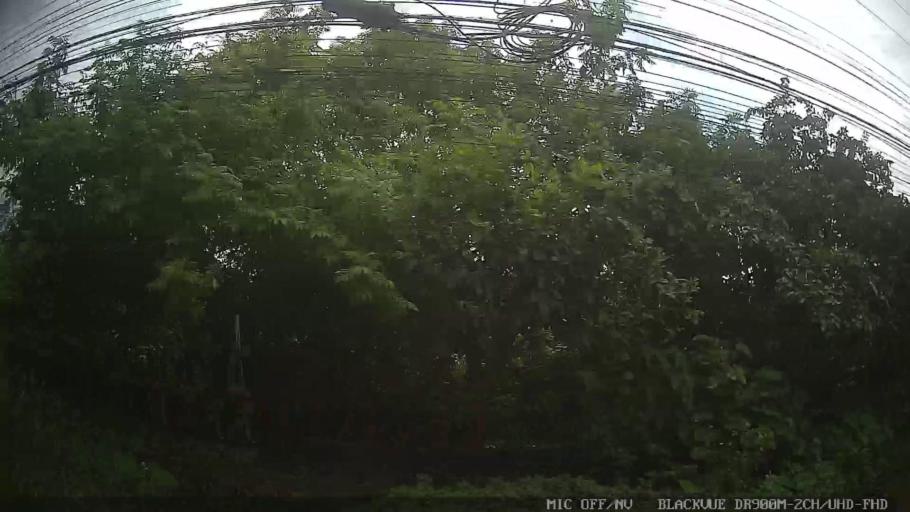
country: BR
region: Sao Paulo
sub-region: Itaquaquecetuba
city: Itaquaquecetuba
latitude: -23.4869
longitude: -46.3084
